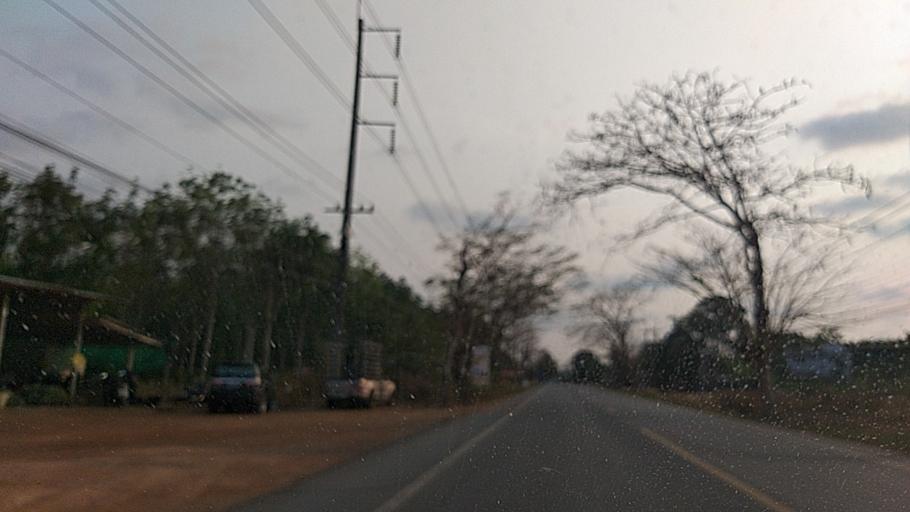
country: TH
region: Trat
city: Khao Saming
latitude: 12.3104
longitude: 102.3512
